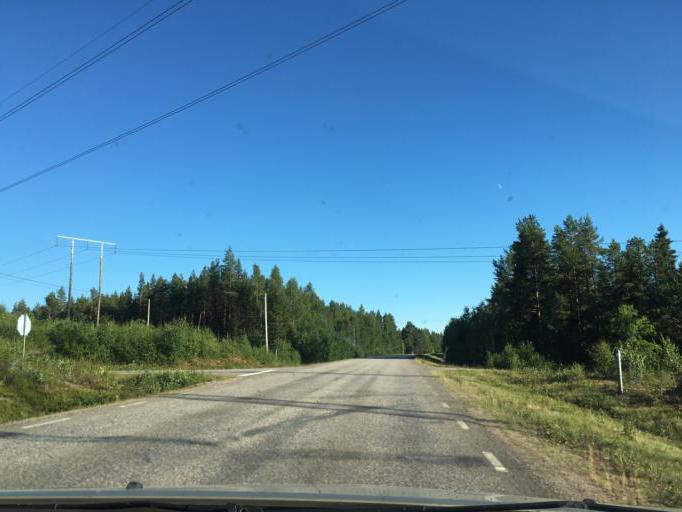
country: SE
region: Norrbotten
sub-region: Kalix Kommun
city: Rolfs
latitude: 65.9098
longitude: 22.9288
